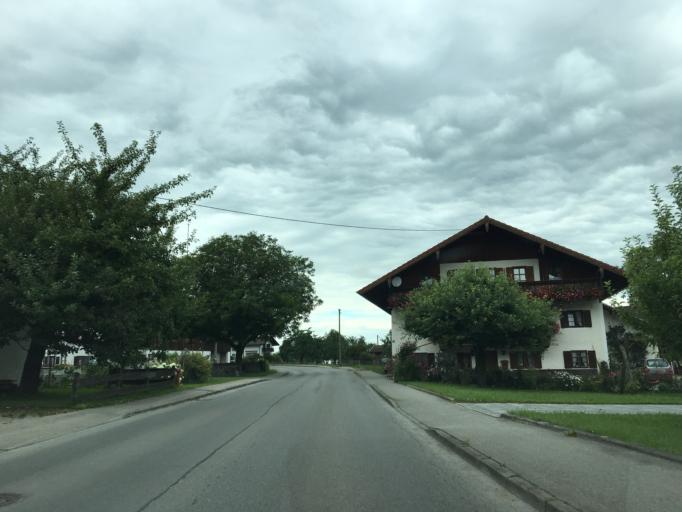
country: DE
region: Bavaria
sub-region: Upper Bavaria
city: Bad Feilnbach
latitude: 47.7638
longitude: 12.0397
